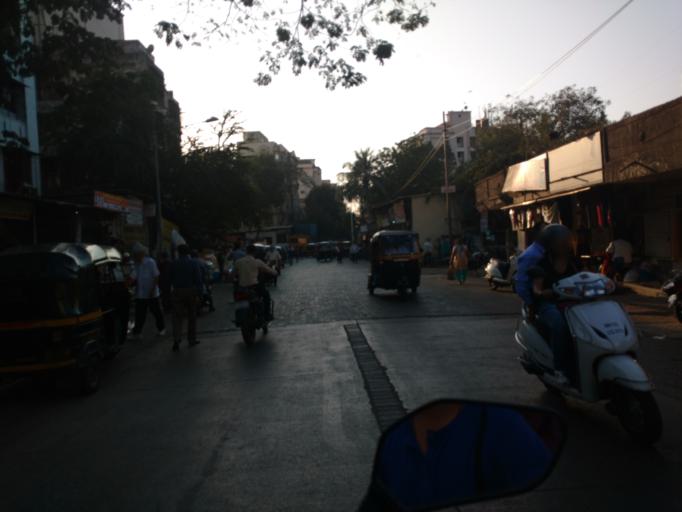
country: IN
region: Maharashtra
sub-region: Mumbai Suburban
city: Borivli
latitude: 19.2034
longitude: 72.8435
